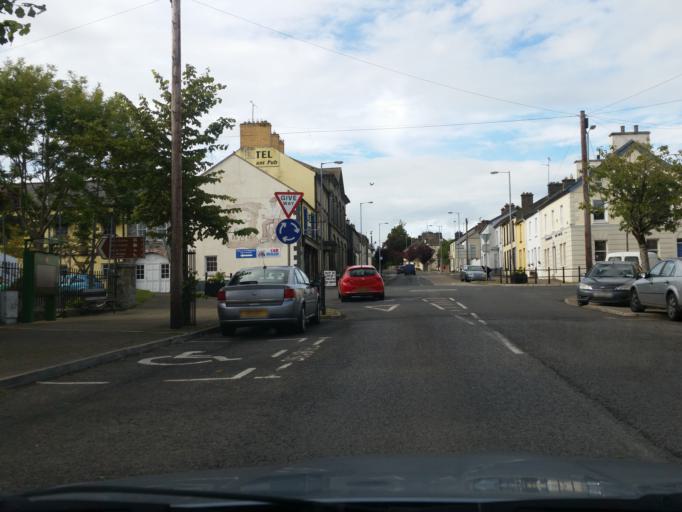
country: GB
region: Northern Ireland
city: Lisnaskea
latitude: 54.1817
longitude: -7.3605
